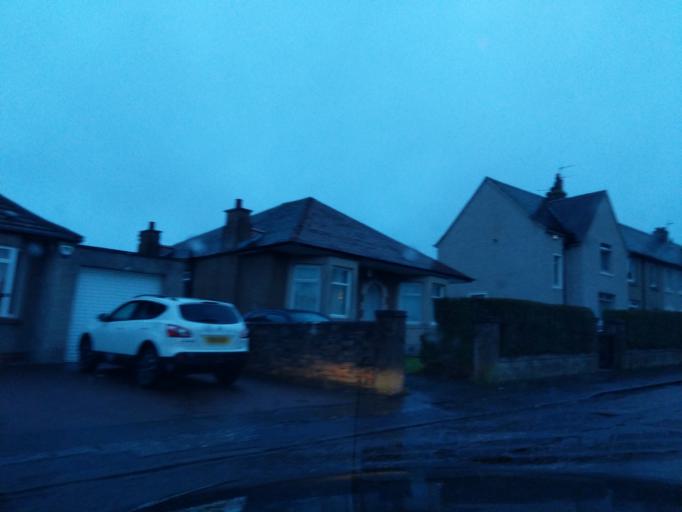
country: GB
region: Scotland
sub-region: Edinburgh
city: Colinton
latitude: 55.9592
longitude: -3.2925
